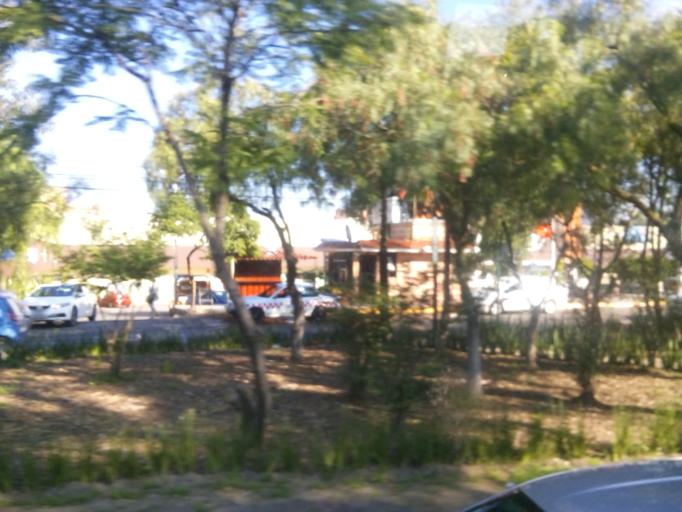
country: MX
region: Mexico
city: Vista Hermosa
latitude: 19.5190
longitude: -99.2464
